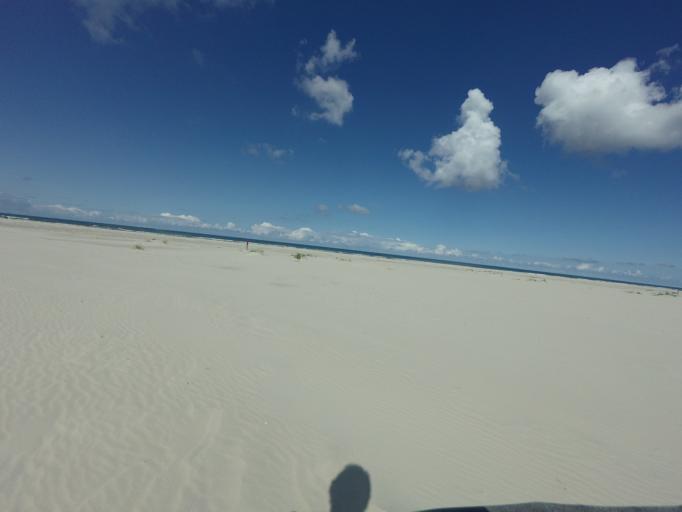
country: NL
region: Friesland
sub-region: Gemeente Terschelling
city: West-Terschelling
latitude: 53.3922
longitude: 5.1999
